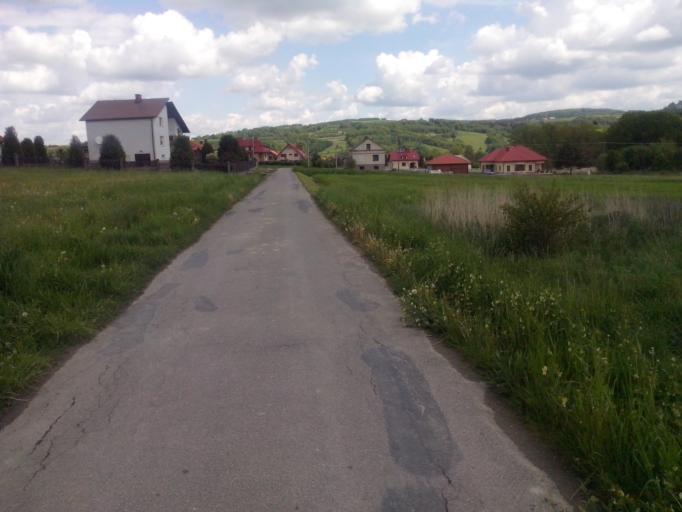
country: PL
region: Subcarpathian Voivodeship
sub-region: Powiat strzyzowski
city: Strzyzow
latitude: 49.8397
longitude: 21.8030
